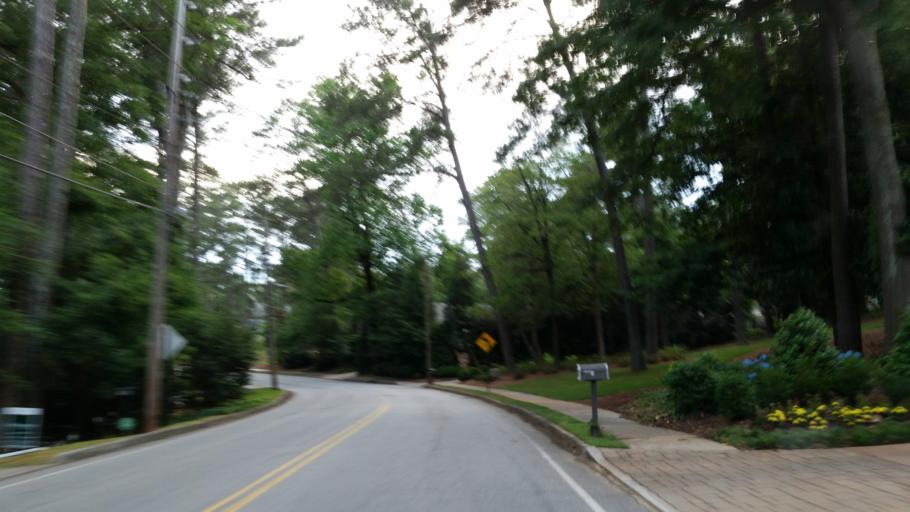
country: US
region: Georgia
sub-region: DeKalb County
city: North Atlanta
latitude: 33.8470
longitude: -84.3939
